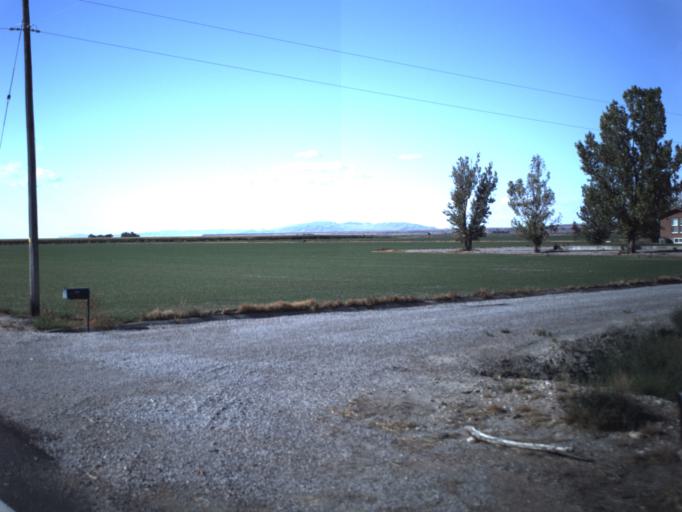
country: US
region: Utah
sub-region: Millard County
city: Delta
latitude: 39.2798
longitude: -112.6529
